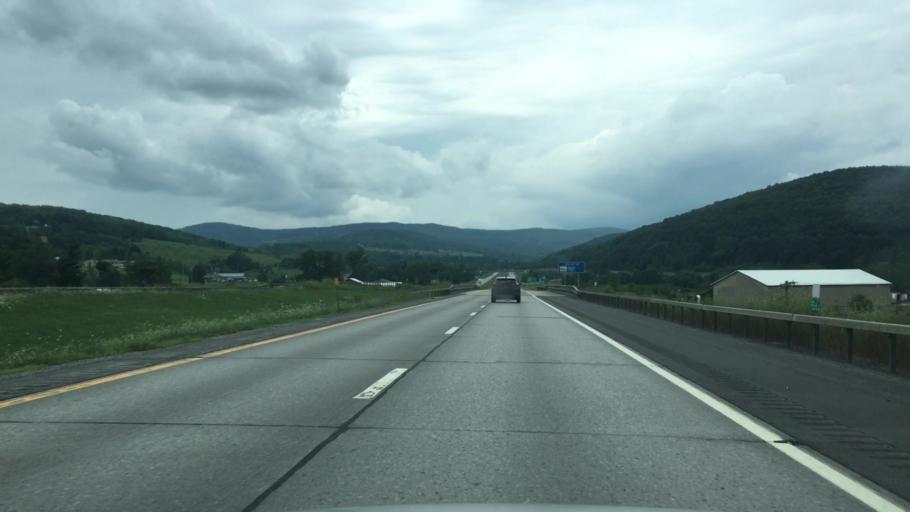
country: US
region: New York
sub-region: Schoharie County
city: Cobleskill
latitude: 42.6466
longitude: -74.5312
